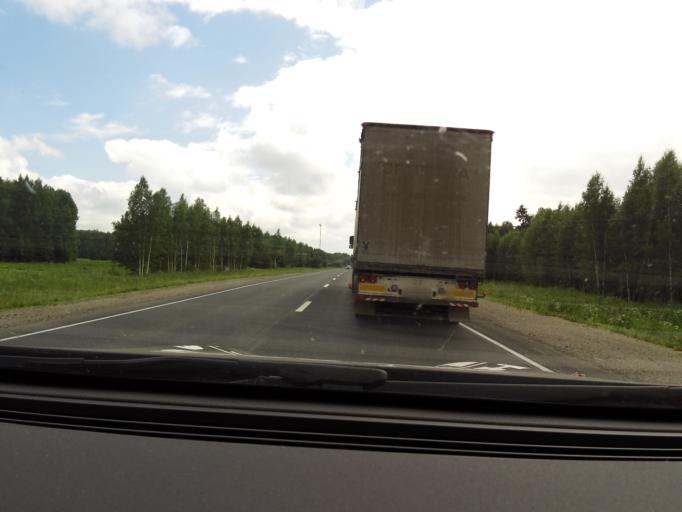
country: RU
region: Perm
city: Orda
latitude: 57.1999
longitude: 57.1082
